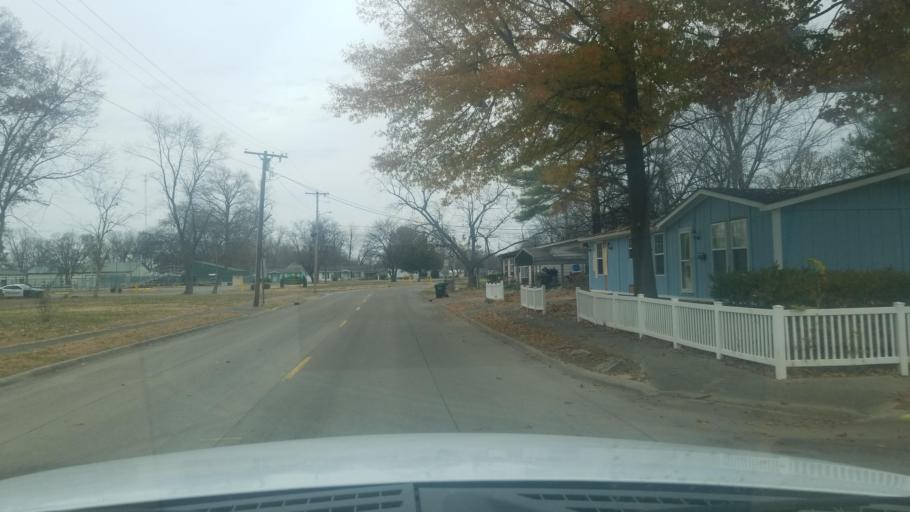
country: US
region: Illinois
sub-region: Saline County
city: Harrisburg
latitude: 37.7345
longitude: -88.5528
